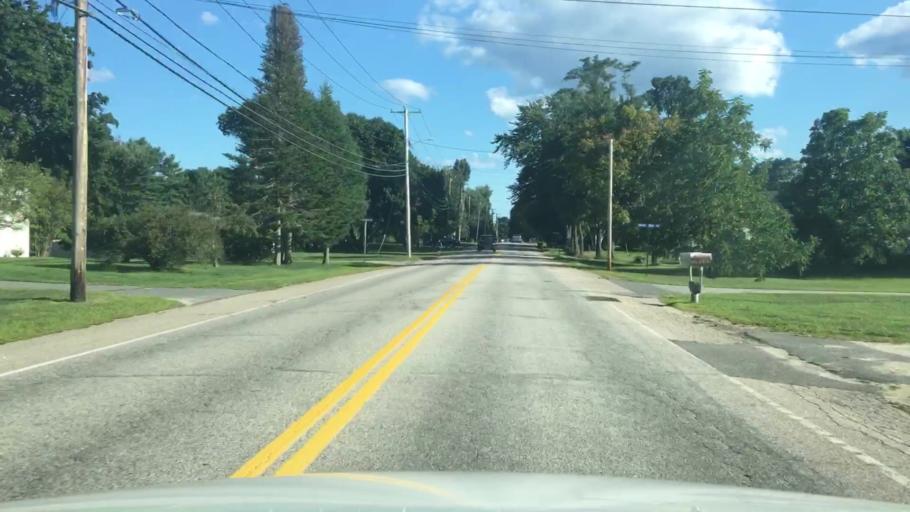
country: US
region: Maine
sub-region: Cumberland County
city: Scarborough
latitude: 43.5689
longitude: -70.3154
